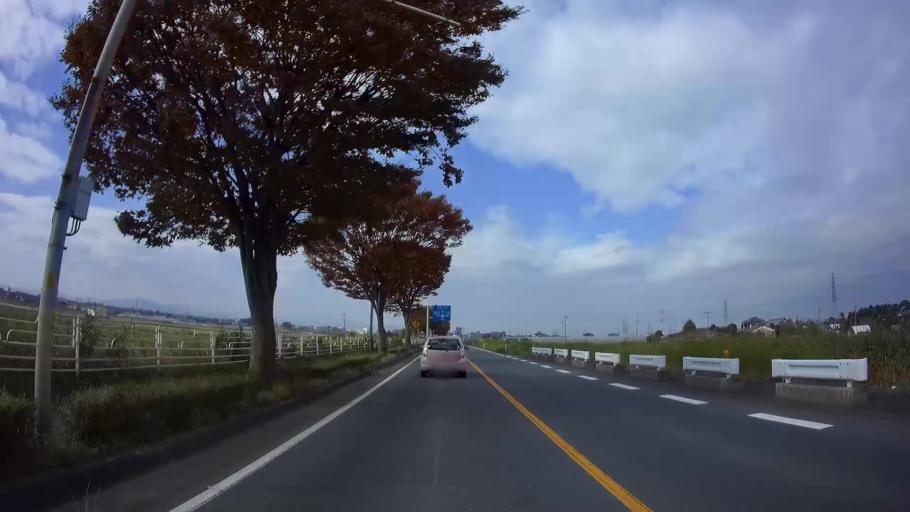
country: JP
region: Saitama
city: Fukayacho
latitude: 36.2167
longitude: 139.2594
